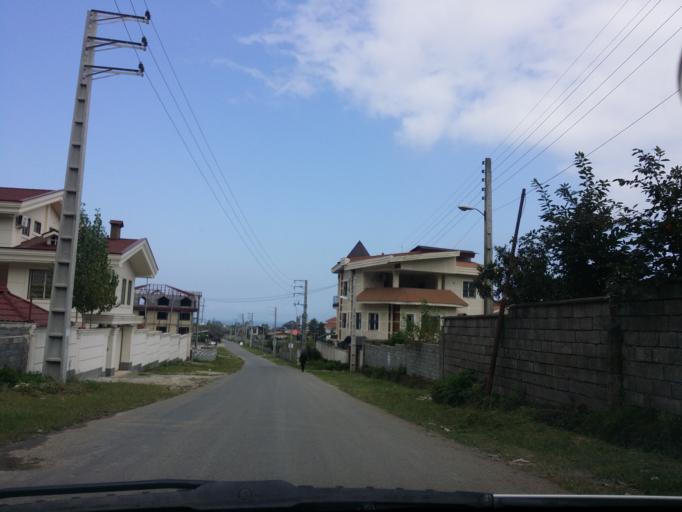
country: IR
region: Mazandaran
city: Chalus
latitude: 36.6512
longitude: 51.3586
